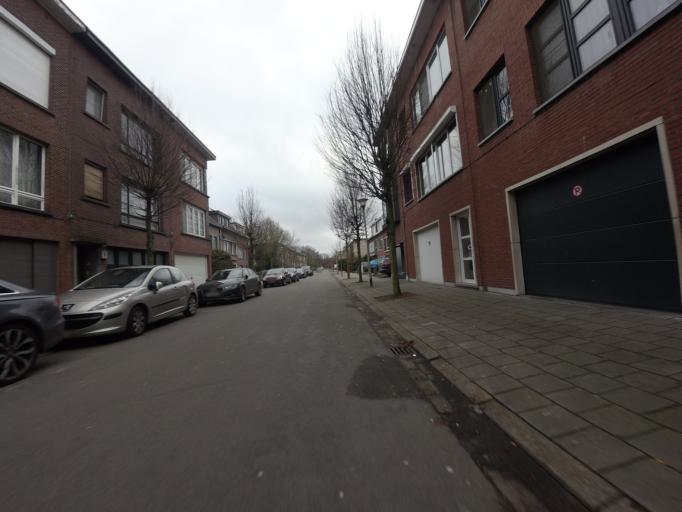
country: BE
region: Flanders
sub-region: Provincie Antwerpen
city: Hoboken
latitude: 51.1725
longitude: 4.3590
